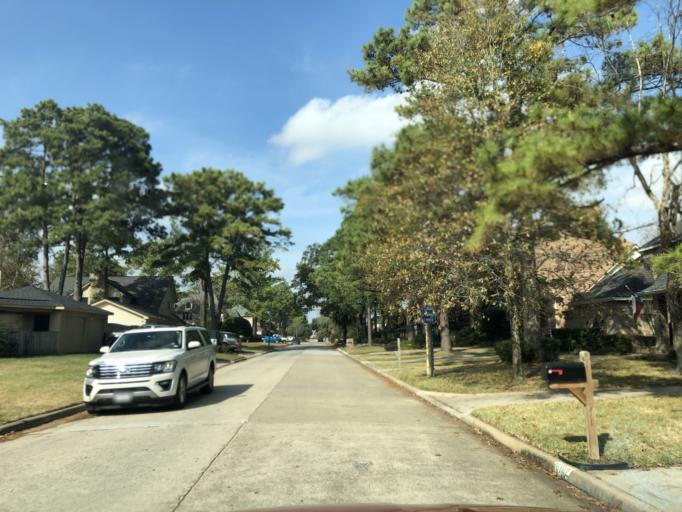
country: US
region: Texas
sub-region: Harris County
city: Tomball
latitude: 30.0306
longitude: -95.5452
